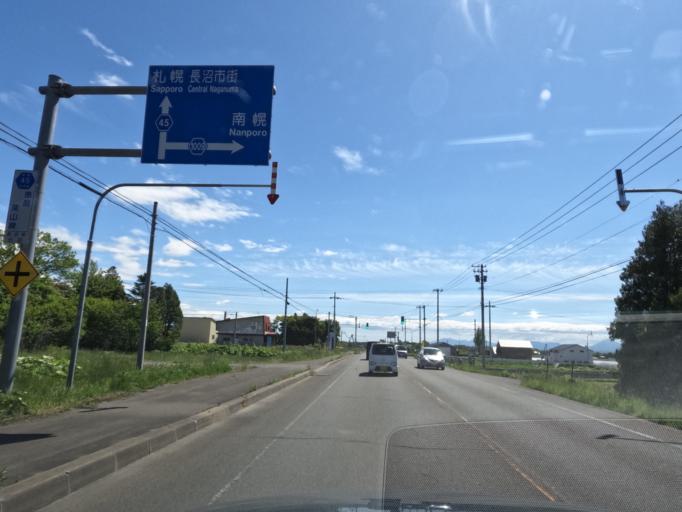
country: JP
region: Hokkaido
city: Kitahiroshima
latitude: 43.0314
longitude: 141.7149
